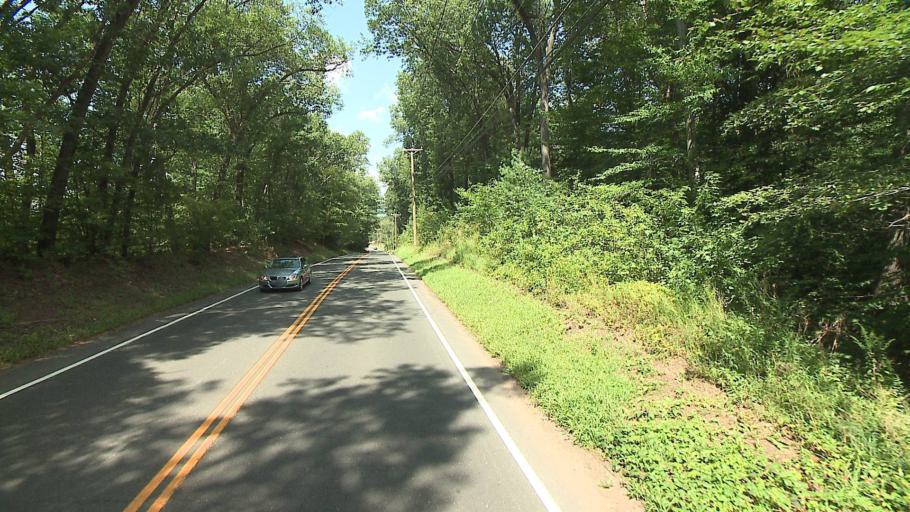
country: US
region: Connecticut
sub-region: Hartford County
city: Broad Brook
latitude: 41.9321
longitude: -72.5114
